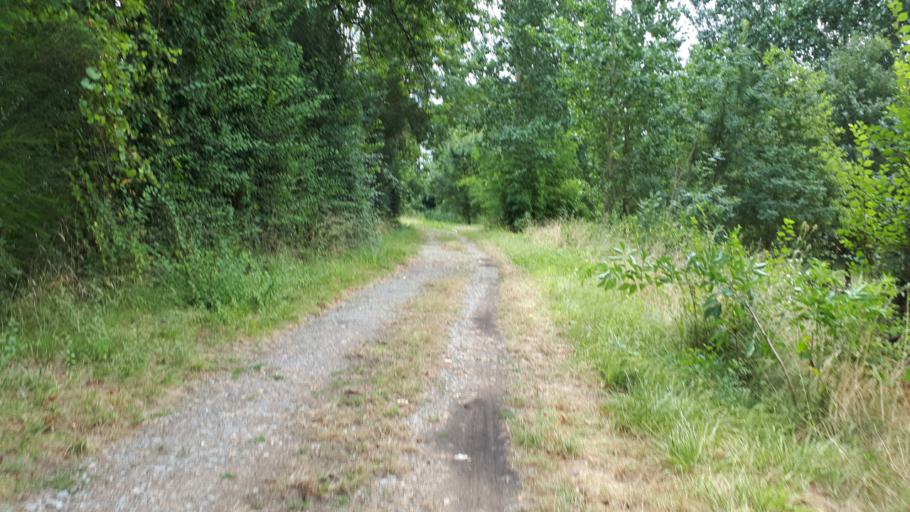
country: FR
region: Pays de la Loire
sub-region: Departement de Maine-et-Loire
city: Rochefort-sur-Loire
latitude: 47.3336
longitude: -0.6903
